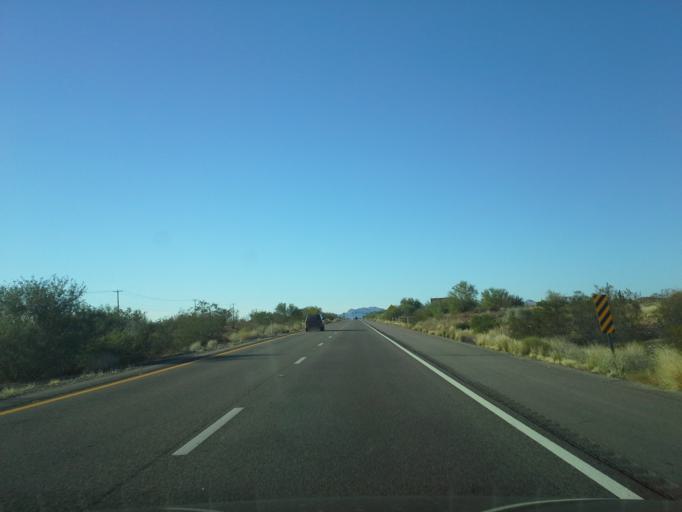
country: US
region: Arizona
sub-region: Pinal County
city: Gold Camp
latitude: 33.3319
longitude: -111.4357
